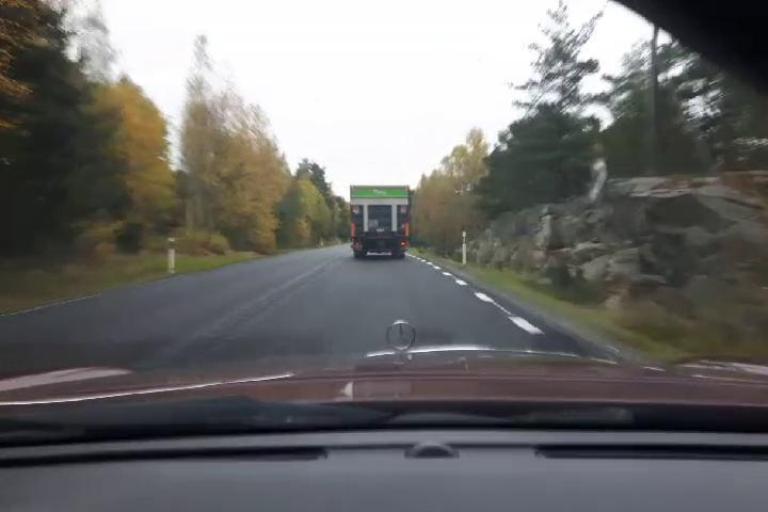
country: SE
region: Soedermanland
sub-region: Strangnas Kommun
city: Strangnas
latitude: 59.4253
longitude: 17.0256
